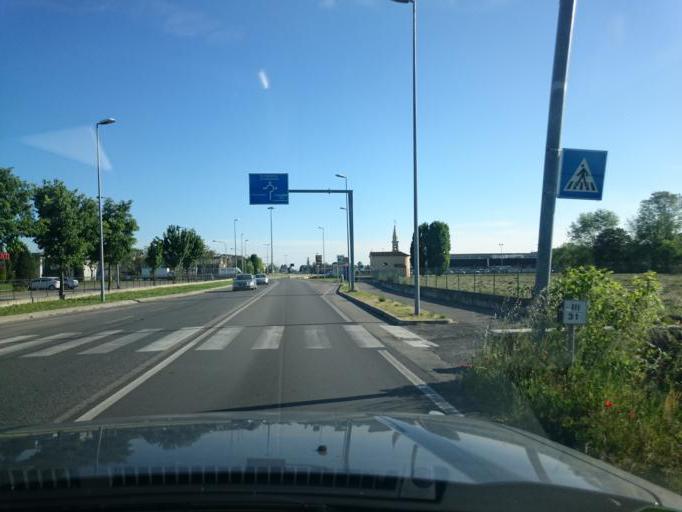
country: IT
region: Veneto
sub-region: Provincia di Venezia
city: Caselle
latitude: 45.4853
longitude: 12.0039
